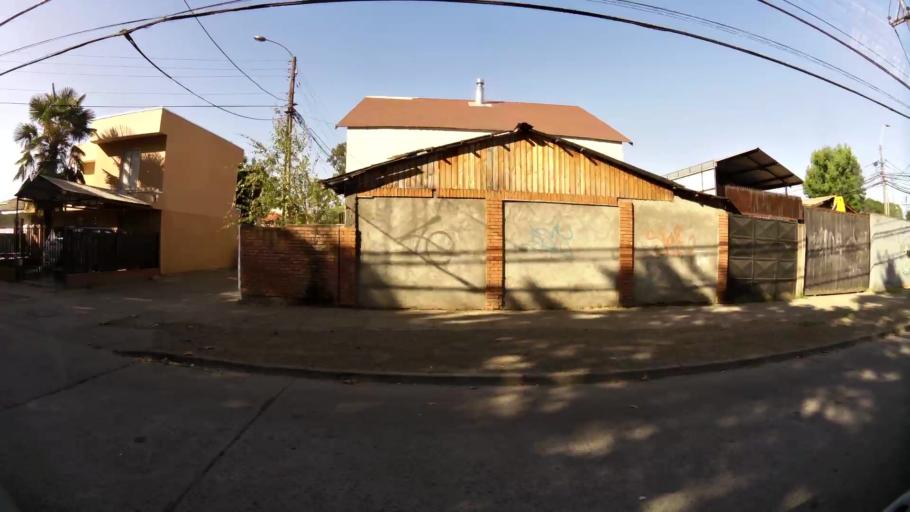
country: CL
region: Maule
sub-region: Provincia de Talca
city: Talca
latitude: -35.4347
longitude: -71.6668
